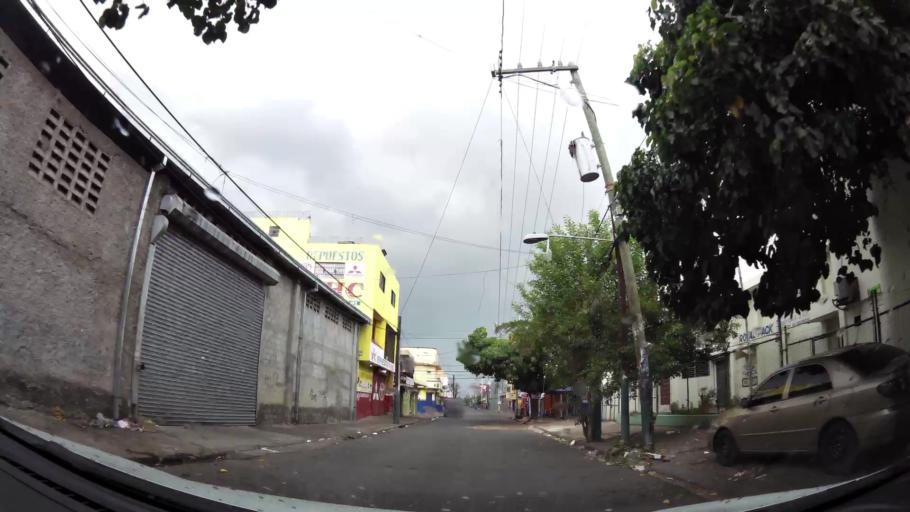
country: DO
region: Nacional
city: San Carlos
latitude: 18.4902
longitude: -69.9078
